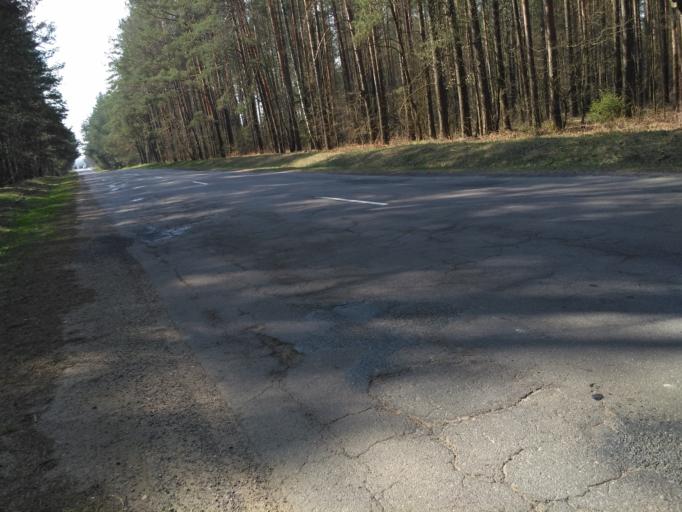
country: BY
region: Minsk
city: Zamostochcha
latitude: 53.8992
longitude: 27.9289
